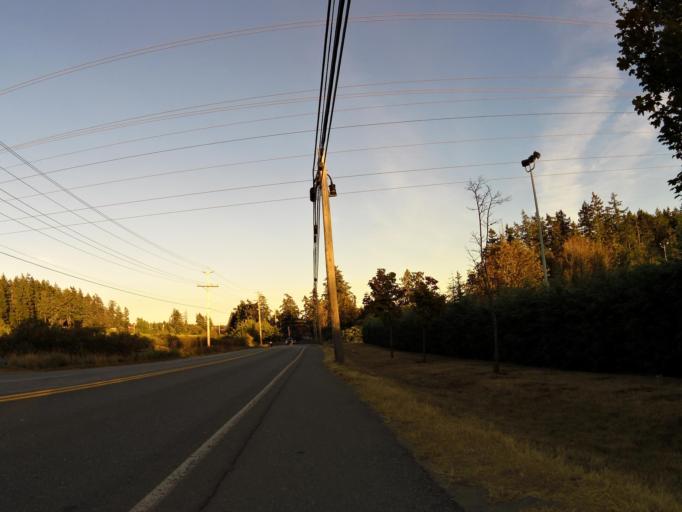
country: CA
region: British Columbia
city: North Cowichan
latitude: 48.8628
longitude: -123.5180
